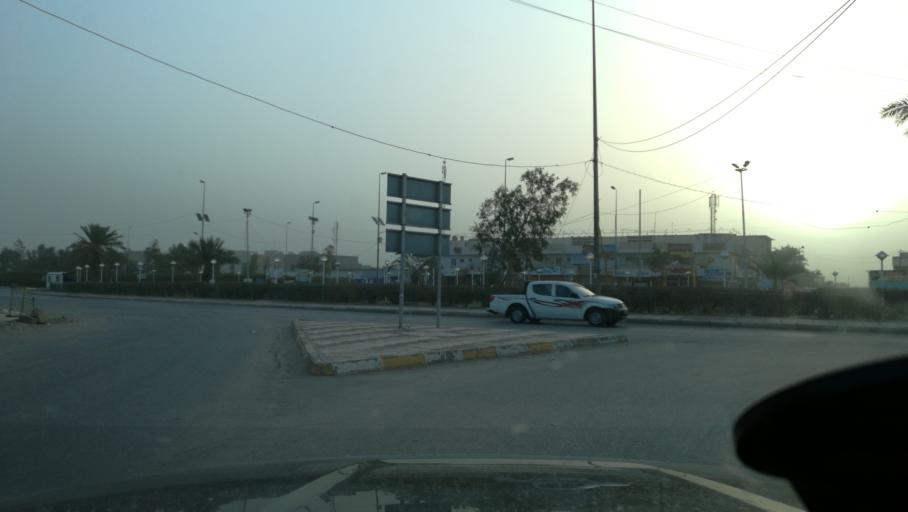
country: IQ
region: Dhi Qar
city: An Nasiriyah
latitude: 31.0401
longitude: 46.2405
